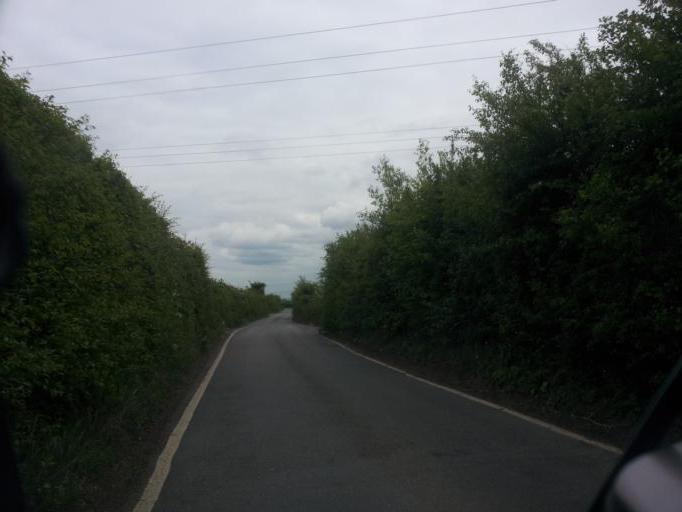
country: GB
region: England
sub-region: Kent
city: Queenborough
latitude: 51.3859
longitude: 0.7222
